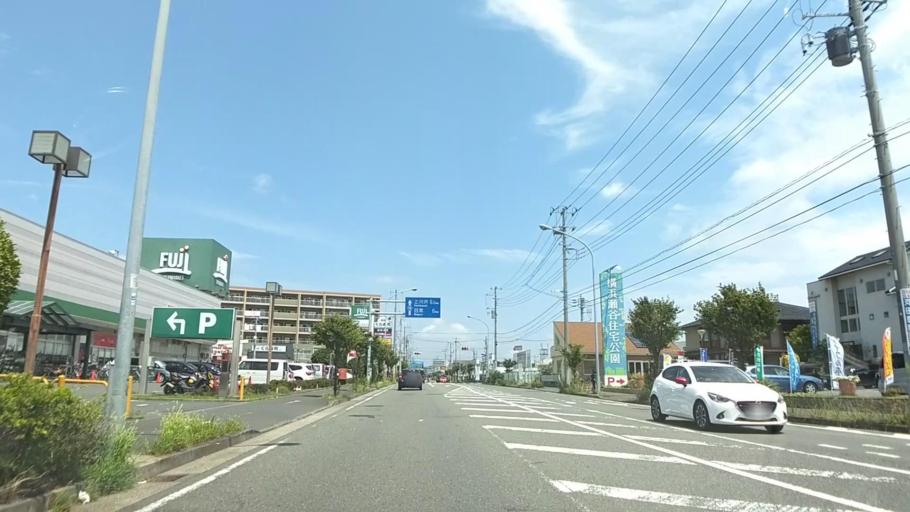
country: JP
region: Kanagawa
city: Minami-rinkan
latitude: 35.4598
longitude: 139.4805
